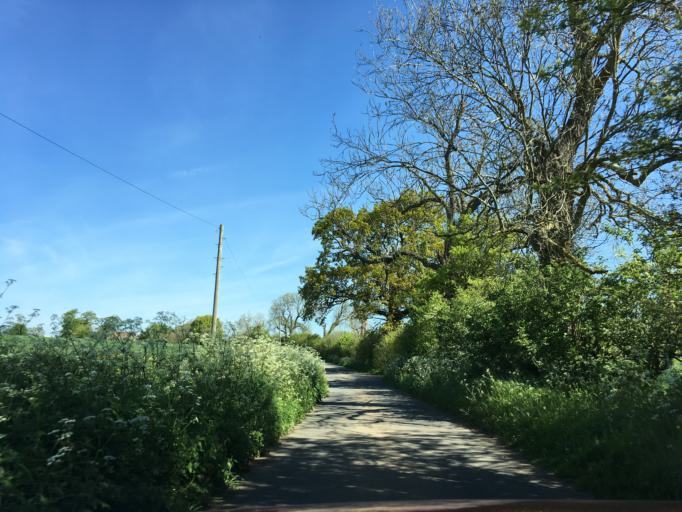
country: GB
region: England
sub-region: Wiltshire
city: Luckington
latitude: 51.5919
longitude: -2.2547
